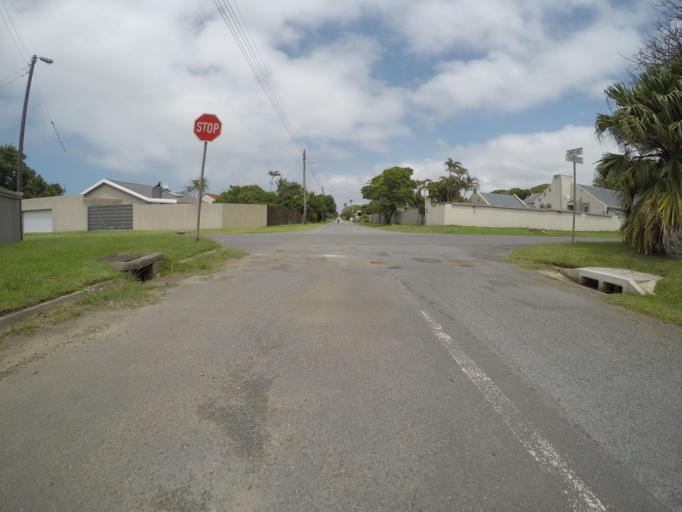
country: ZA
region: Eastern Cape
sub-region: Buffalo City Metropolitan Municipality
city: East London
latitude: -32.9419
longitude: 28.0124
